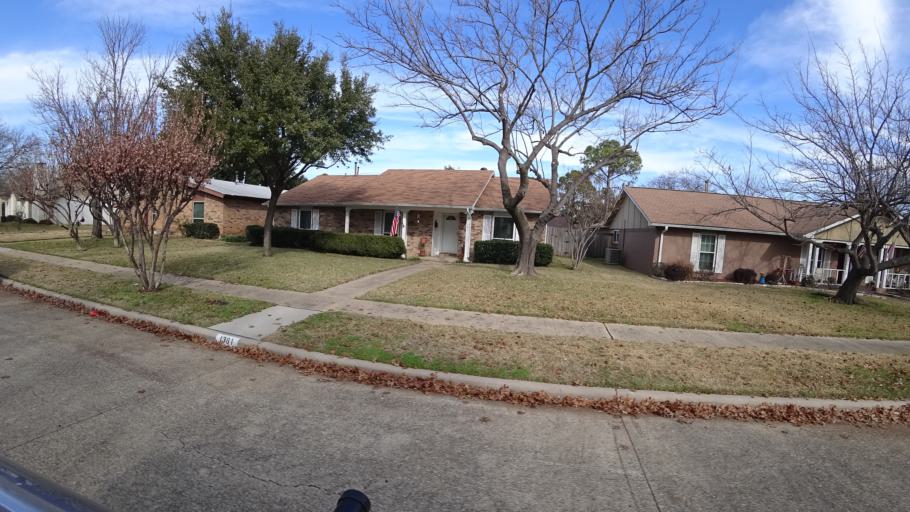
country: US
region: Texas
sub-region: Denton County
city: Lewisville
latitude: 33.0445
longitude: -97.0289
